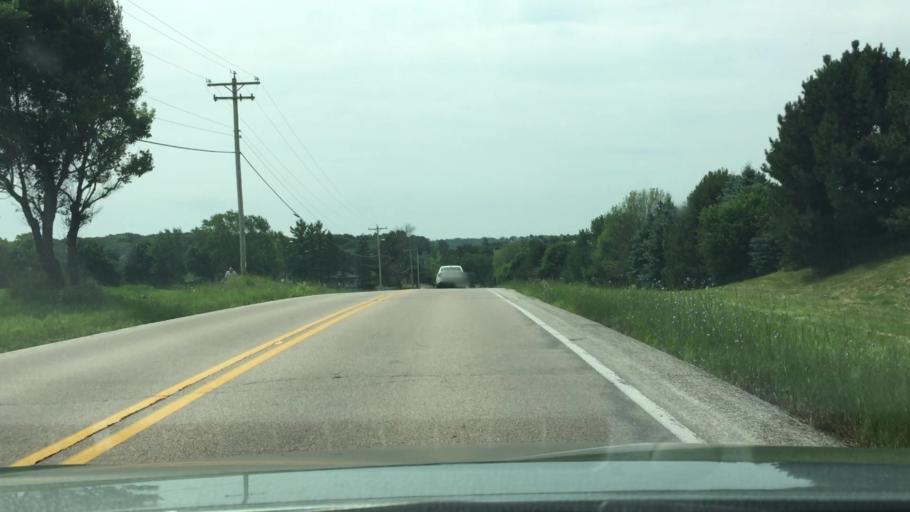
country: US
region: Wisconsin
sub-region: Waukesha County
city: Hartland
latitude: 43.1162
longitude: -88.3132
